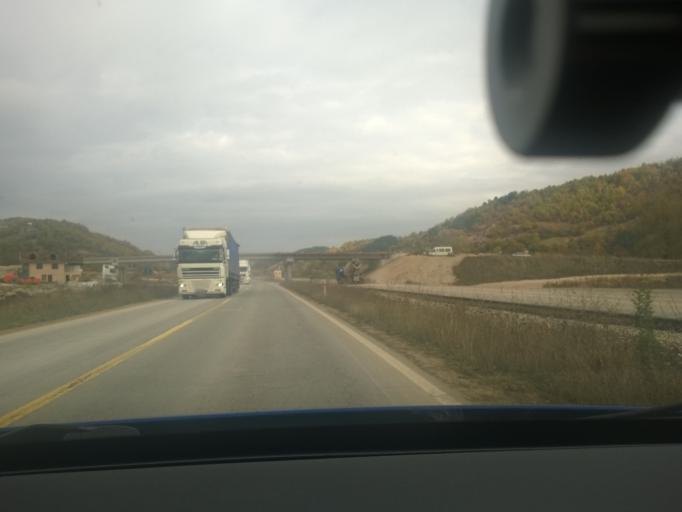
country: RS
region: Central Serbia
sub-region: Pirotski Okrug
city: Pirot
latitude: 43.1889
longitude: 22.5647
